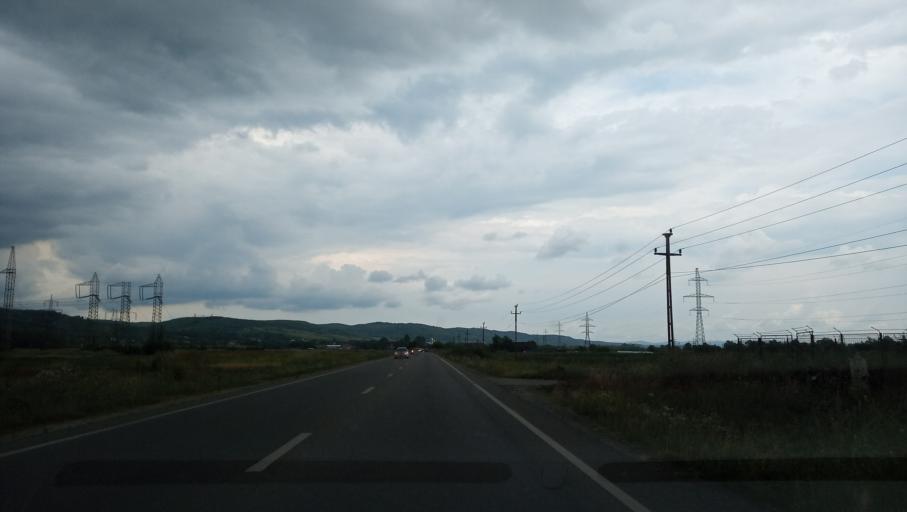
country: RO
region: Gorj
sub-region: Oras Rovinari
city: Rovinari
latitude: 44.9008
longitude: 23.1827
